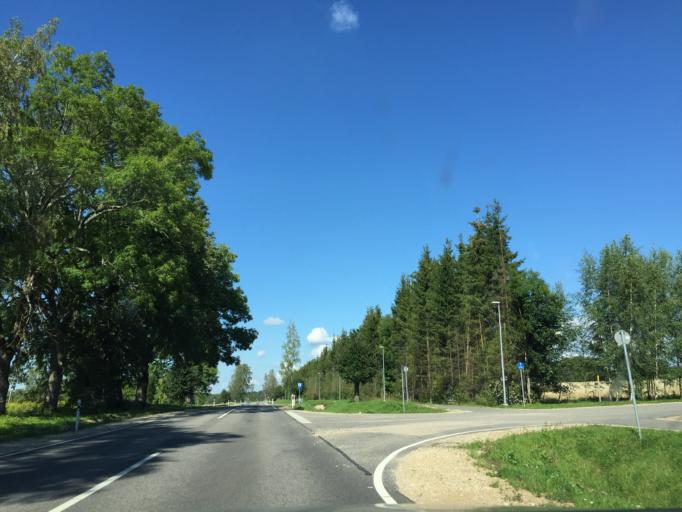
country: LV
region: Limbazu Rajons
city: Limbazi
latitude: 57.4924
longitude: 24.7089
